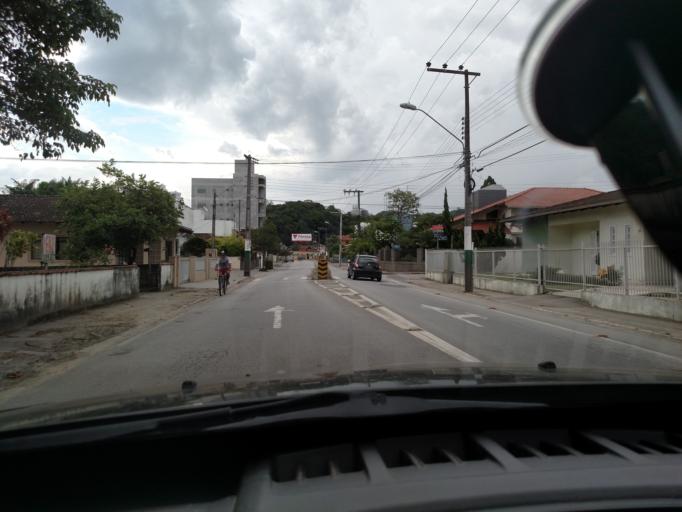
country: BR
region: Santa Catarina
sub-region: Brusque
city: Brusque
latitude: -27.0832
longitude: -48.9136
